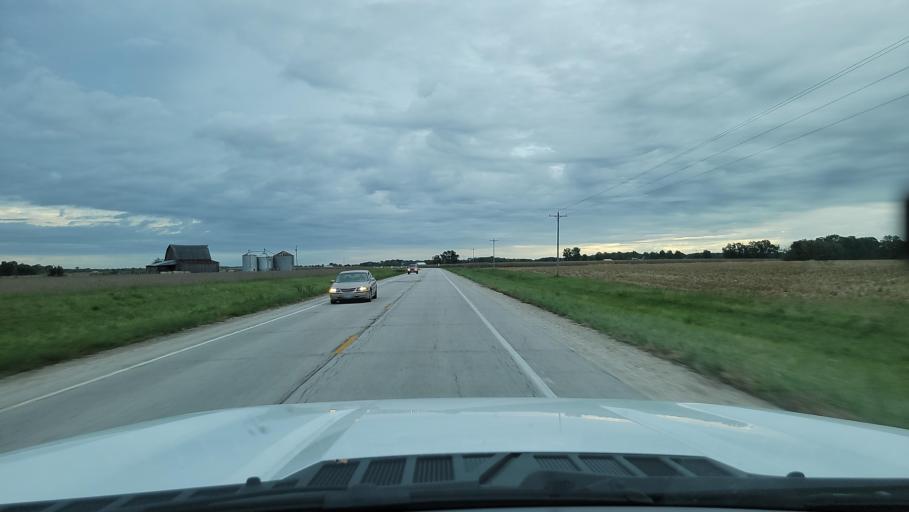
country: US
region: Illinois
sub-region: Schuyler County
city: Rushville
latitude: 40.0951
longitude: -90.6034
